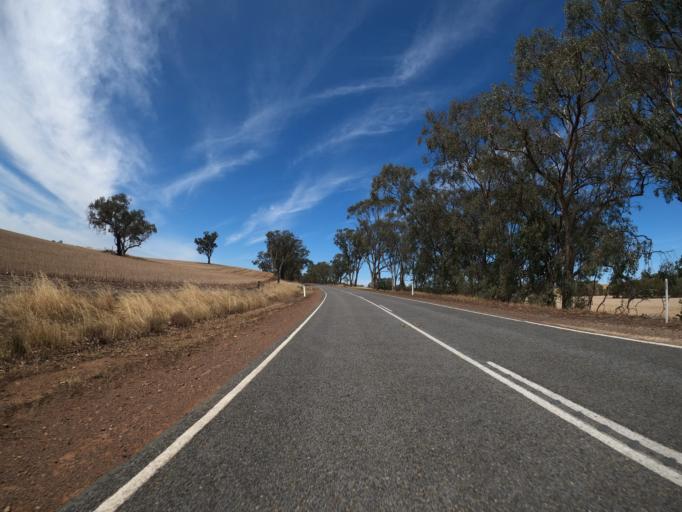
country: AU
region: Victoria
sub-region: Benalla
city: Benalla
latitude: -36.3356
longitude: 145.9592
